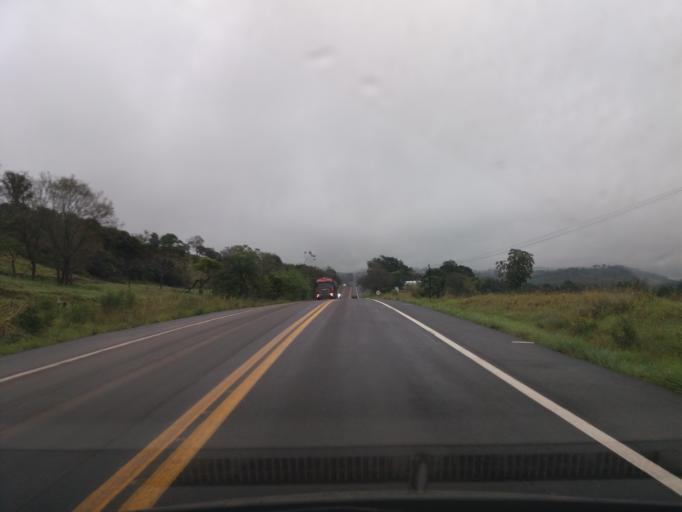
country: BR
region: Parana
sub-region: Realeza
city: Realeza
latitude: -25.5699
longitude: -53.5718
